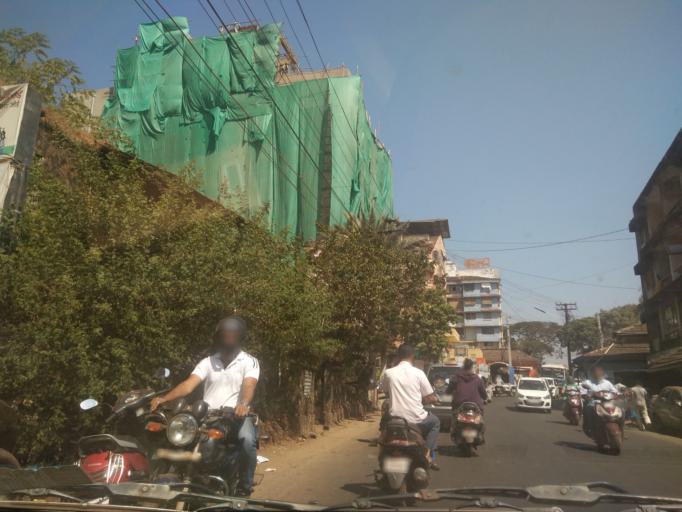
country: IN
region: Goa
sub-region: North Goa
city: Mapuca
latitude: 15.5922
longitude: 73.8130
